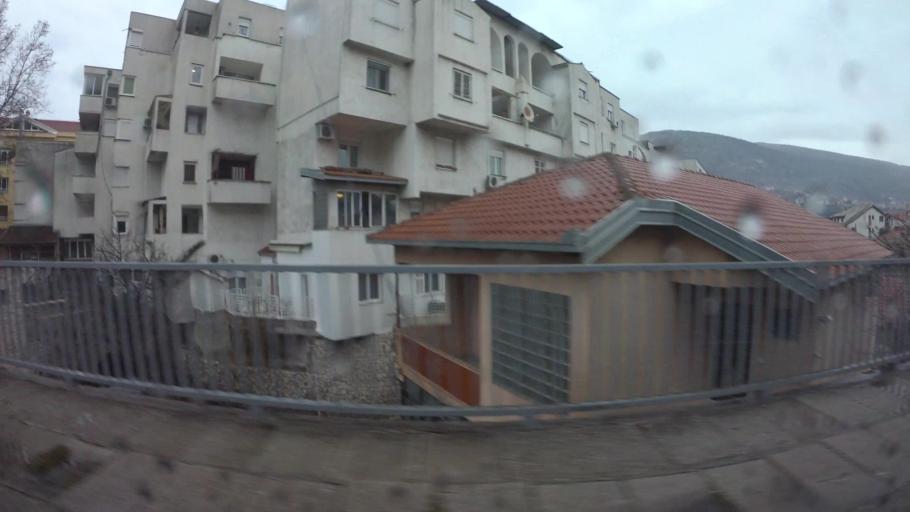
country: BA
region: Federation of Bosnia and Herzegovina
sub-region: Hercegovacko-Bosanski Kanton
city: Mostar
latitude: 43.3369
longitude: 17.8109
